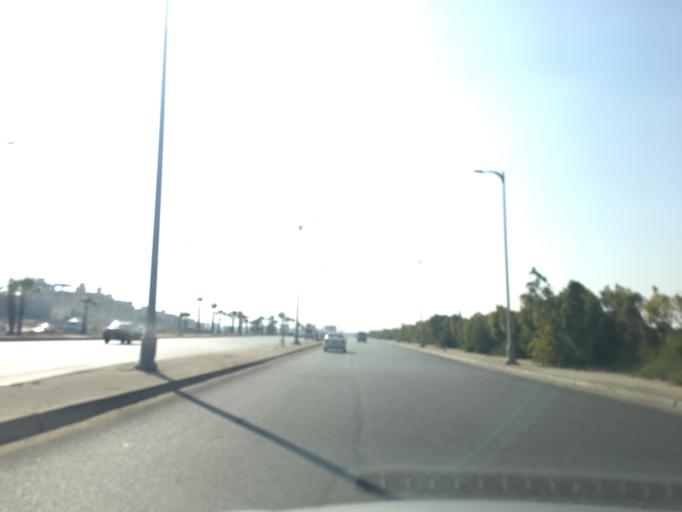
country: EG
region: Al Jizah
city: Madinat Sittah Uktubar
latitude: 29.9932
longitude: 30.9574
